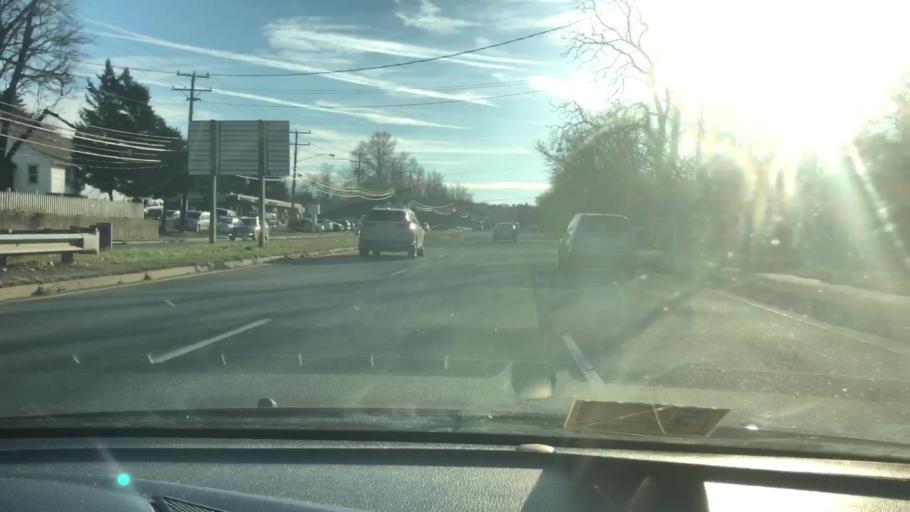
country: US
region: Virginia
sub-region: Fairfax County
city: Huntington
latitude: 38.7957
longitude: -77.0821
